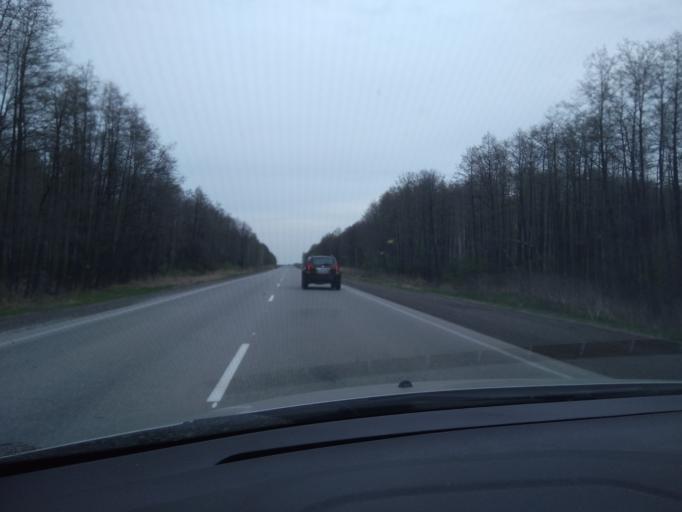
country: RU
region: Sverdlovsk
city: Pyshma
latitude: 56.8832
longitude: 62.9982
